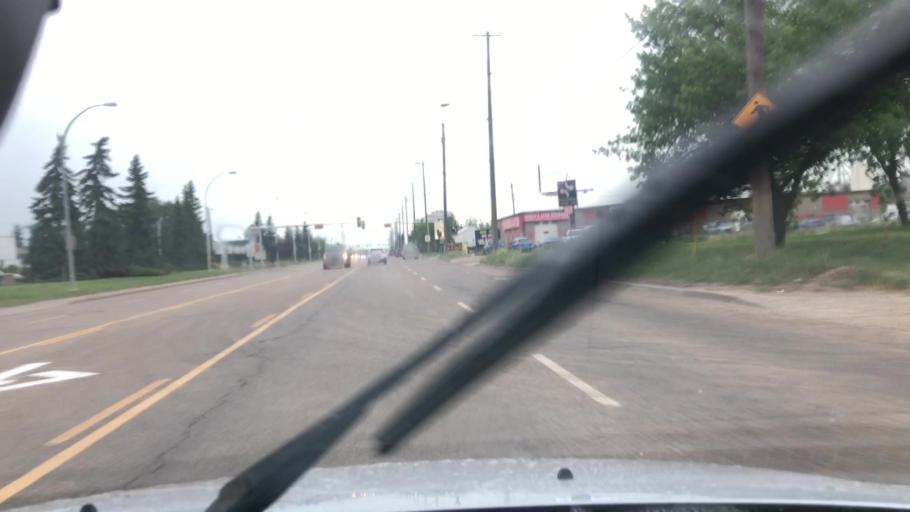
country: CA
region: Alberta
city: St. Albert
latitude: 53.5755
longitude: -113.5779
